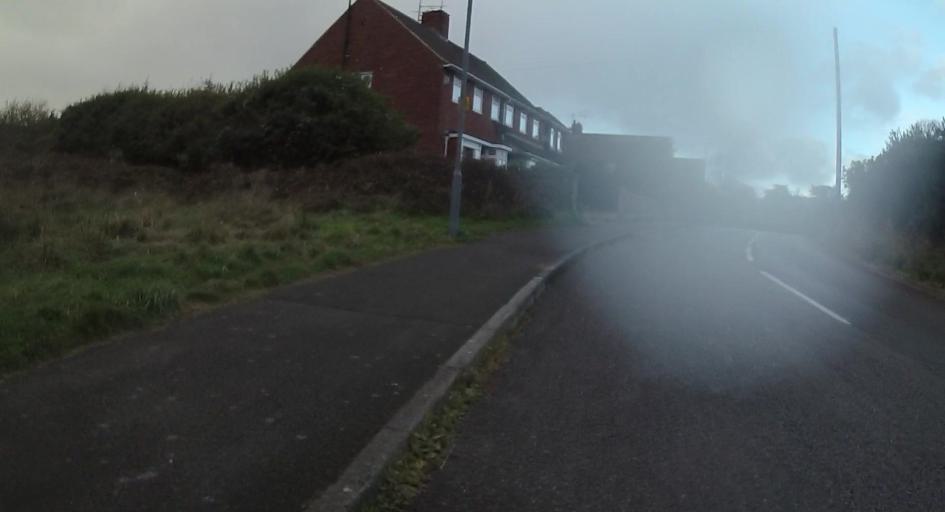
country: GB
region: England
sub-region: Bracknell Forest
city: Crowthorne
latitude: 51.3644
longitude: -0.7793
